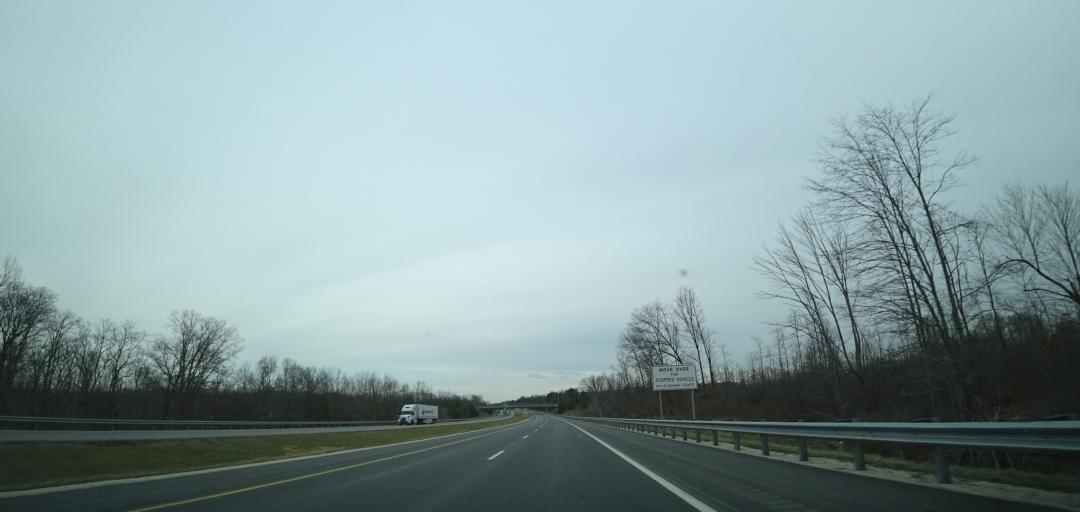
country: US
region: Ohio
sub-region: Mahoning County
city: Austintown
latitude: 41.0961
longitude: -80.8273
